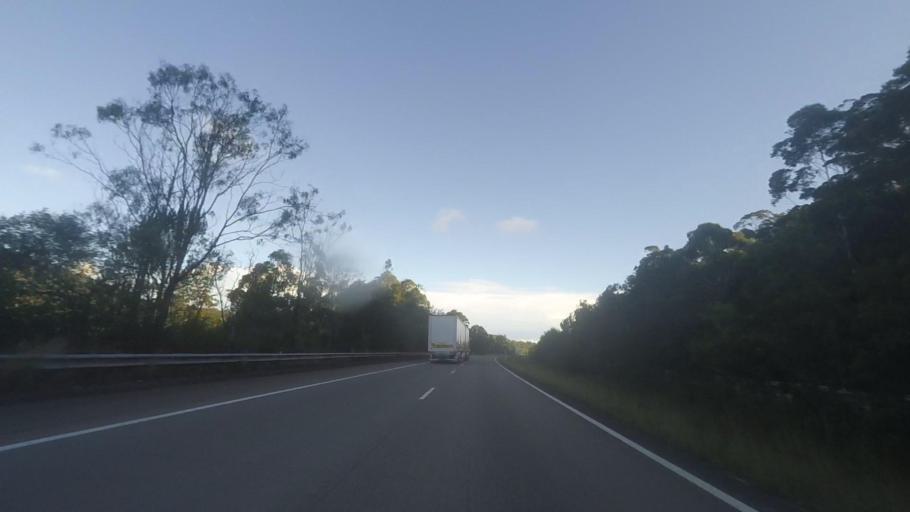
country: AU
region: New South Wales
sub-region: Great Lakes
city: Bulahdelah
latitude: -32.2863
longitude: 152.3403
